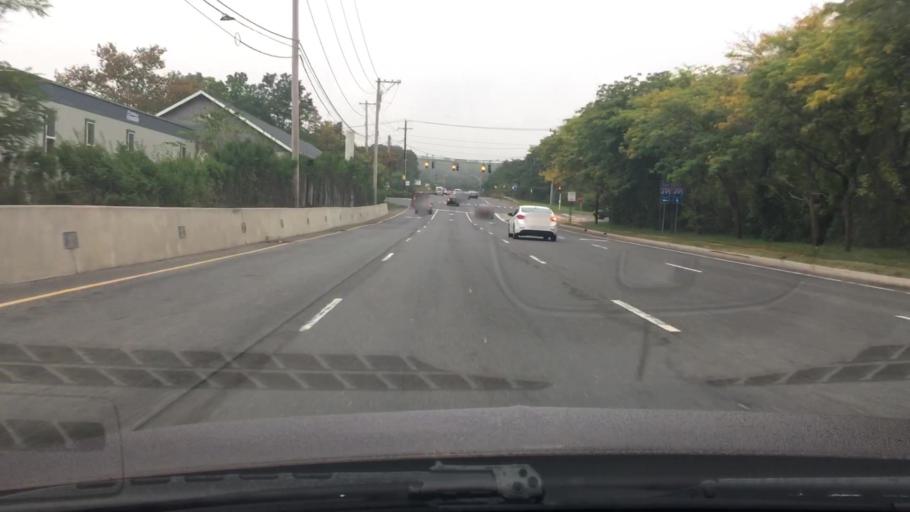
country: US
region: New York
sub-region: Suffolk County
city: Melville
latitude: 40.7821
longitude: -73.4226
